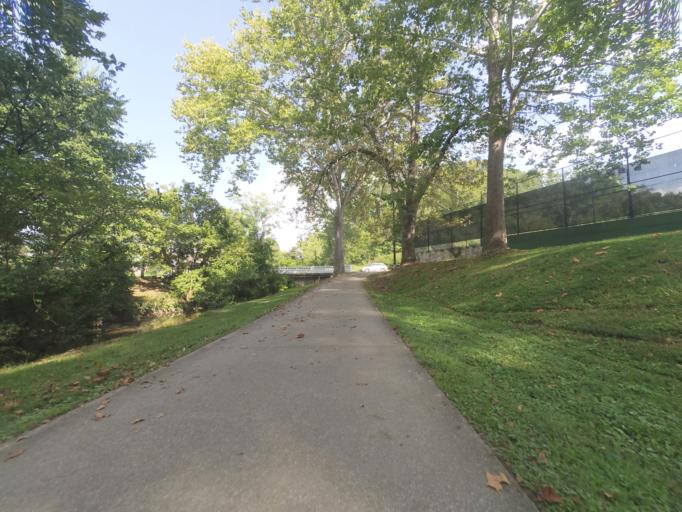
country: US
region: West Virginia
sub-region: Cabell County
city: Huntington
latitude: 38.4074
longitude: -82.4352
